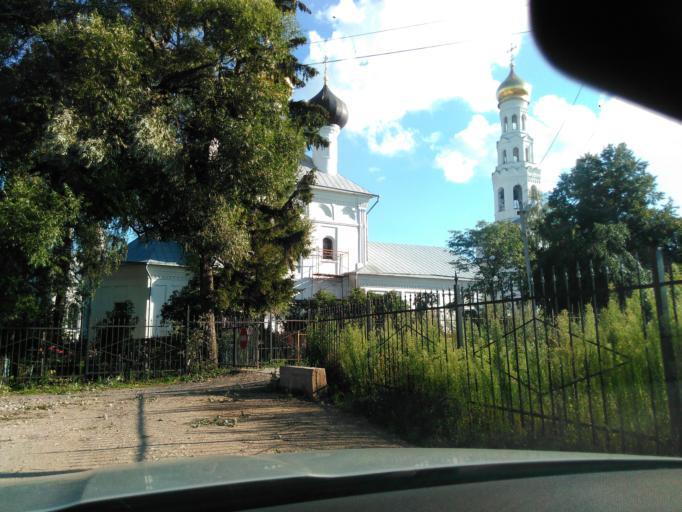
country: RU
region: Tverskaya
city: Zavidovo
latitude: 56.5304
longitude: 36.5310
